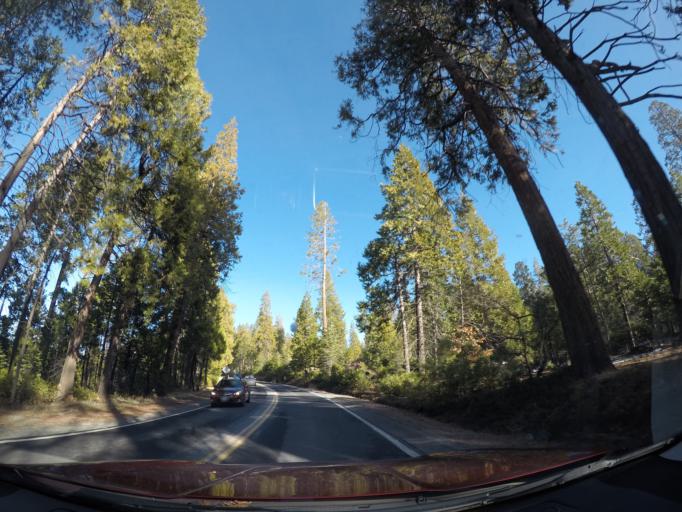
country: US
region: California
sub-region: Tuolumne County
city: Twain Harte
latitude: 38.0625
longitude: -120.1975
